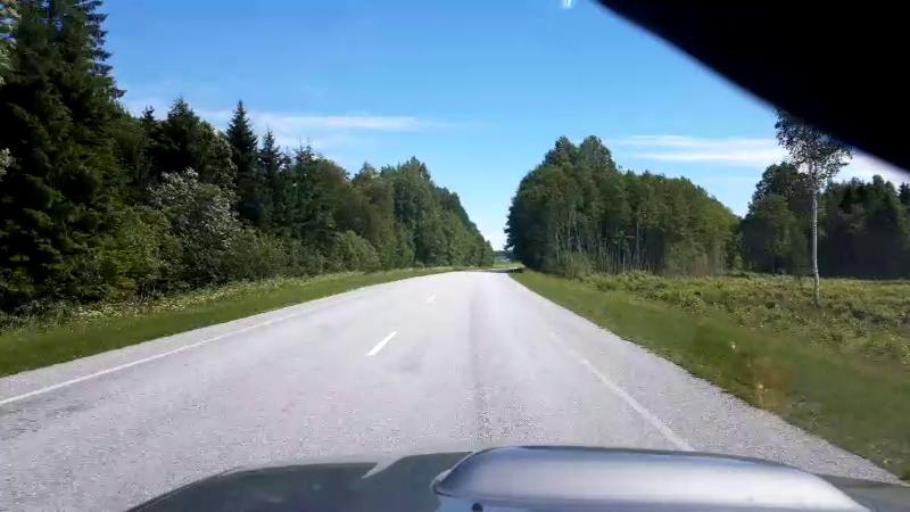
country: EE
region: Laeaene-Virumaa
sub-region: Rakke vald
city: Rakke
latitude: 58.9608
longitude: 26.1622
